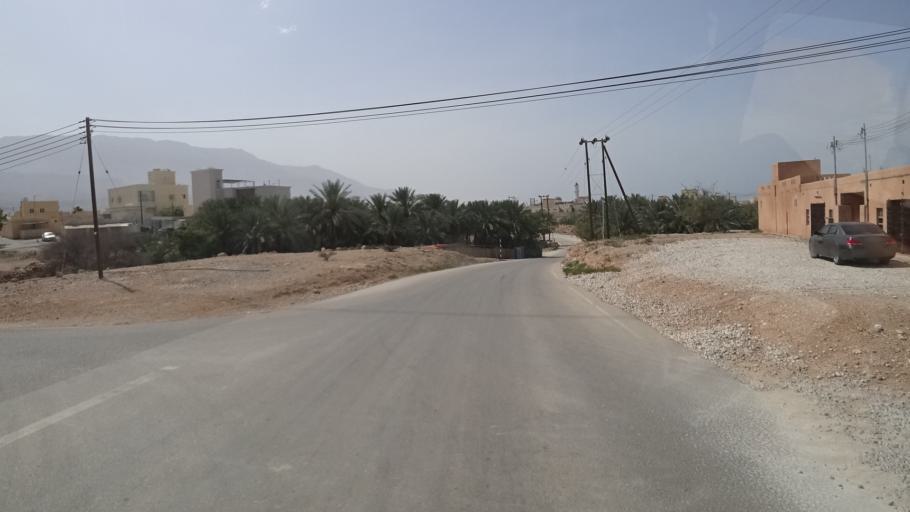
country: OM
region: Ash Sharqiyah
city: Sur
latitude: 22.9889
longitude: 59.1392
